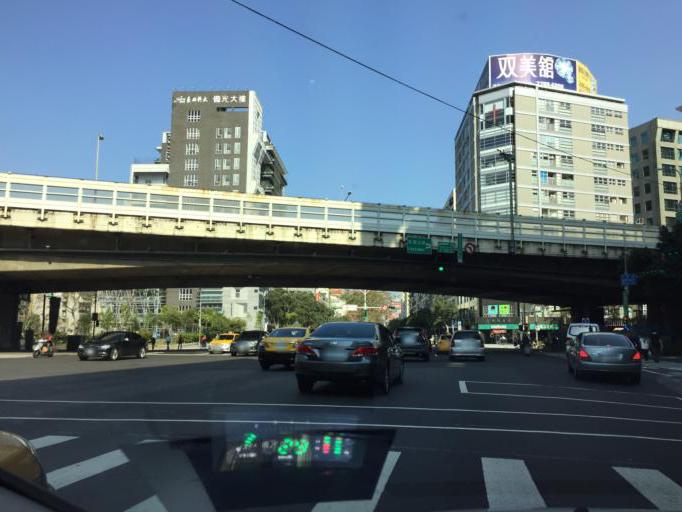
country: TW
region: Taipei
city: Taipei
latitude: 25.0418
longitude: 121.5365
